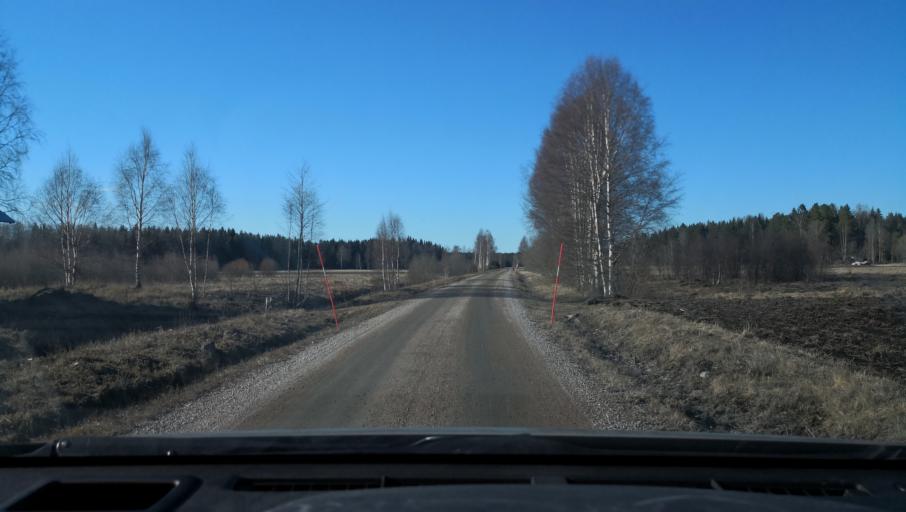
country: SE
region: Vaestmanland
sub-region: Sala Kommun
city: Sala
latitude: 60.1237
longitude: 16.6570
